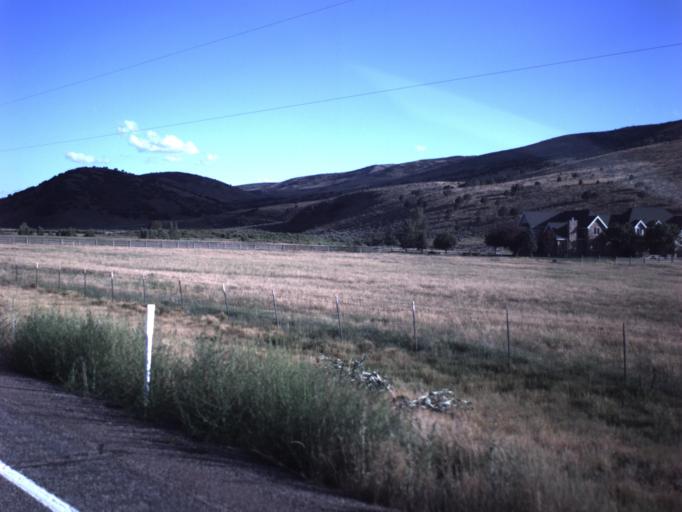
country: US
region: Utah
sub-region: Utah County
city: Woodland Hills
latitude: 39.8746
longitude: -111.5387
